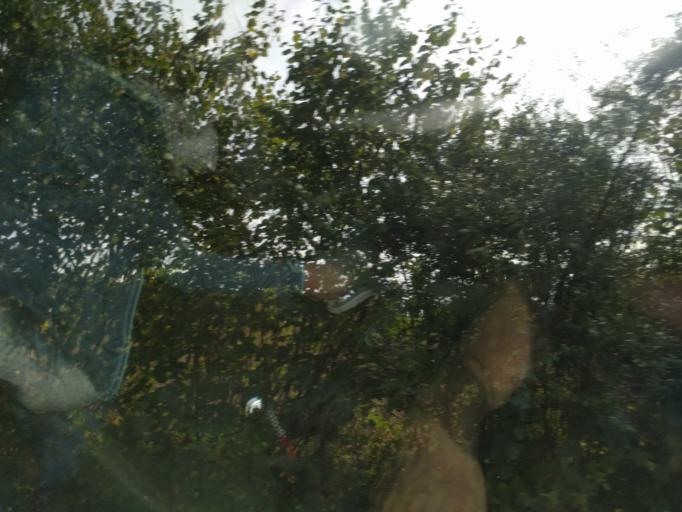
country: DE
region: Schleswig-Holstein
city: Wesenberg
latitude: 53.8389
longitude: 10.5250
